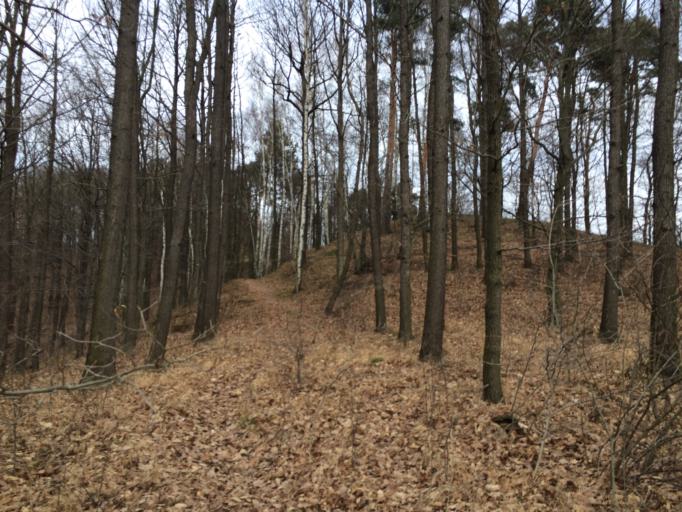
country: PL
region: Lower Silesian Voivodeship
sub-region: Powiat lwowecki
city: Lwowek Slaski
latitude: 51.1578
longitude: 15.5750
